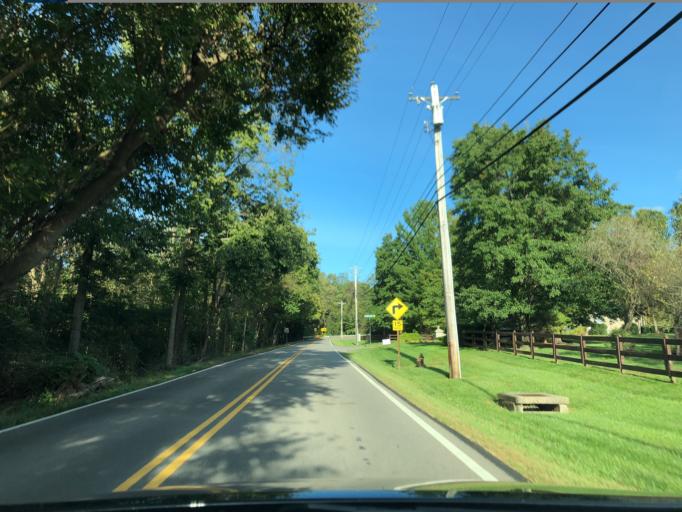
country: US
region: Ohio
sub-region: Hamilton County
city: Loveland
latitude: 39.2579
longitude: -84.2702
